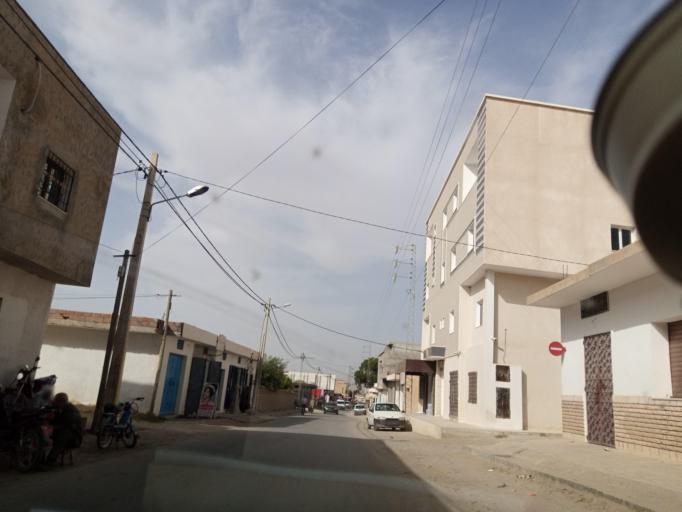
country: TN
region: Al Qasrayn
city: Kasserine
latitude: 35.2138
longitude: 8.8971
